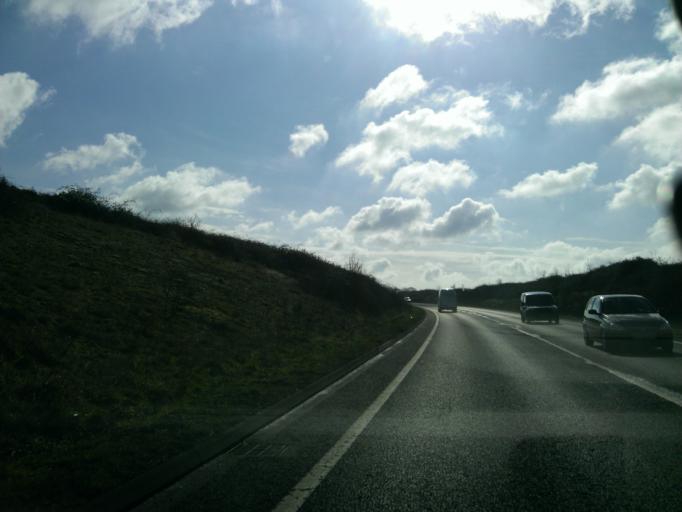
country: GB
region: England
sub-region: Essex
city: Little Clacton
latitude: 51.8423
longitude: 1.1123
